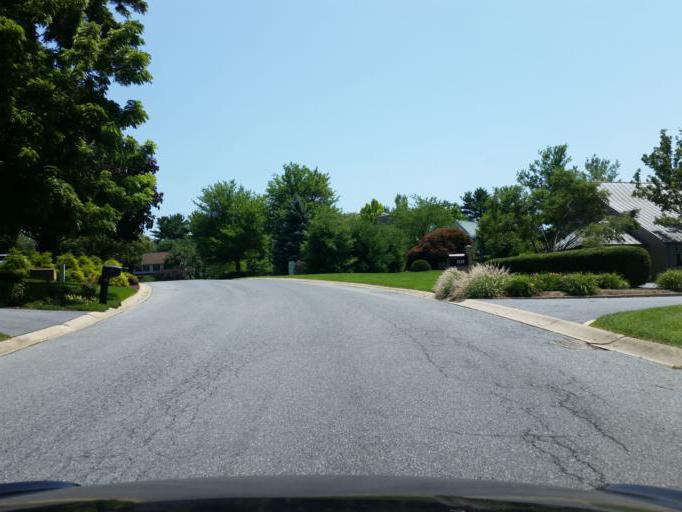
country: US
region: Pennsylvania
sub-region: Lancaster County
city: East Petersburg
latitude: 40.0761
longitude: -76.3208
